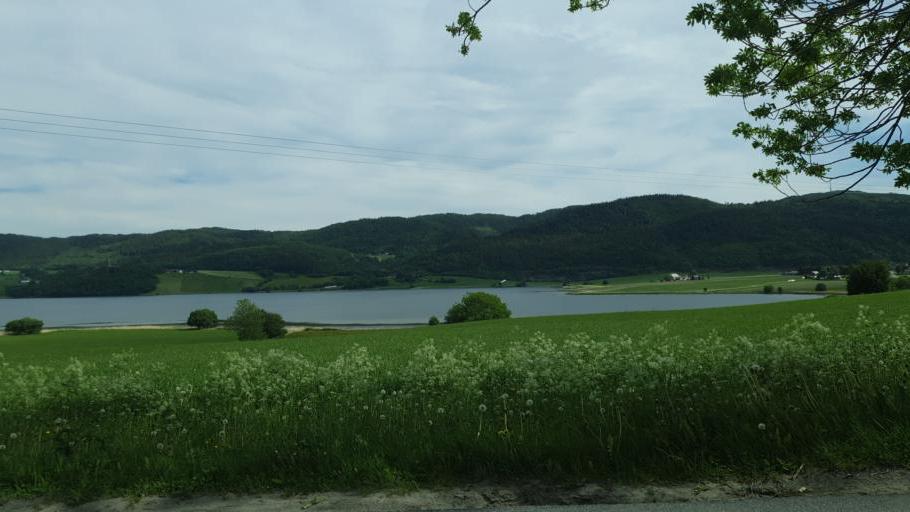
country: NO
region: Sor-Trondelag
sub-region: Rissa
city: Rissa
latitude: 63.5667
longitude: 9.9283
